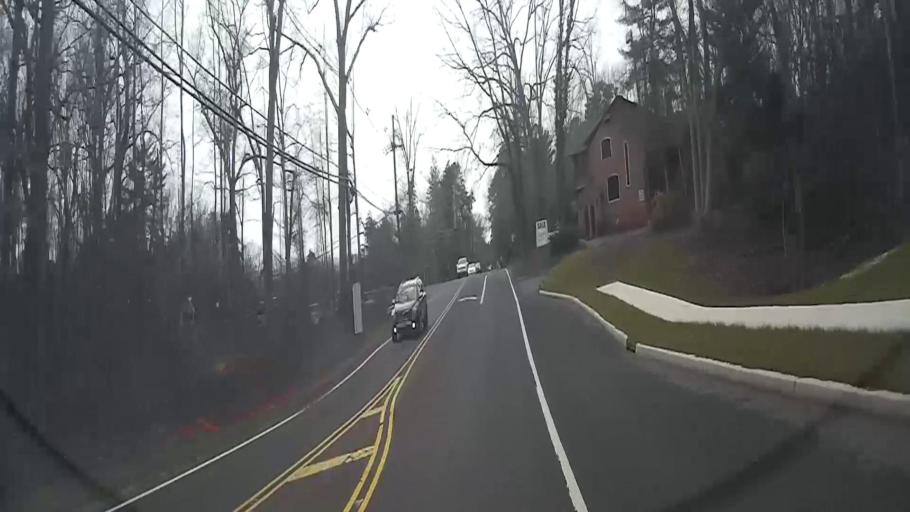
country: US
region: New Jersey
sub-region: Burlington County
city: Medford Lakes
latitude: 39.8673
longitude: -74.8479
